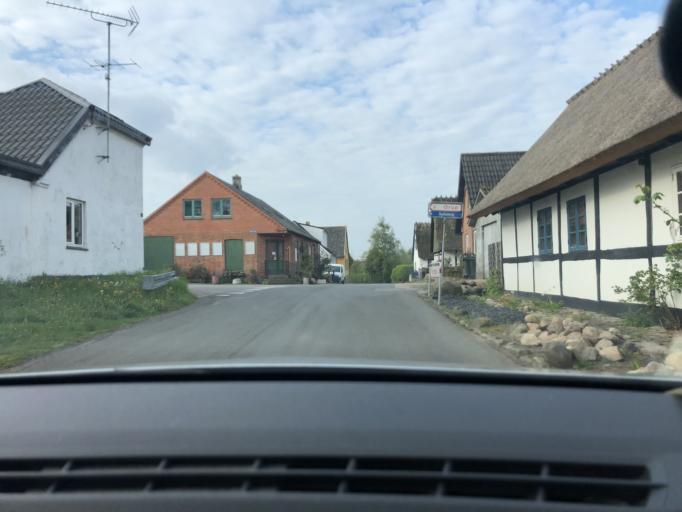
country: DK
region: Zealand
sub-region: Faxe Kommune
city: Ronnede
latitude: 55.2232
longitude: 12.0526
